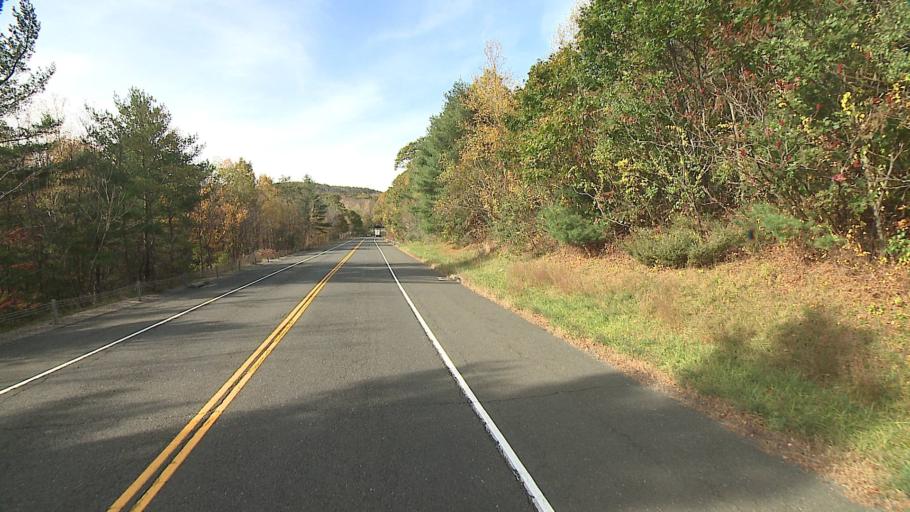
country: US
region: Connecticut
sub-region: Litchfield County
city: Winchester Center
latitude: 41.9419
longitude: -73.1099
